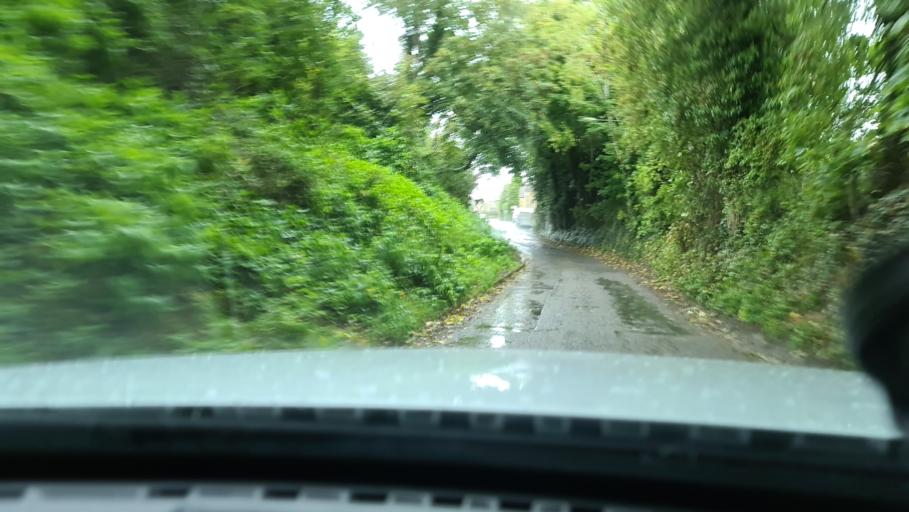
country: GB
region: England
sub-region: Oxfordshire
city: Deddington
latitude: 51.9278
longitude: -1.3689
